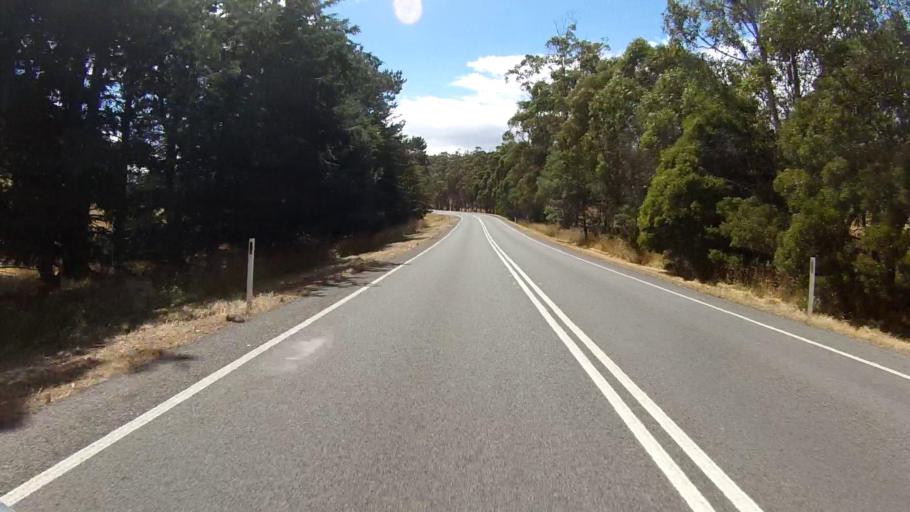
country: AU
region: Tasmania
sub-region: Sorell
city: Sorell
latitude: -42.6276
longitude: 147.6306
